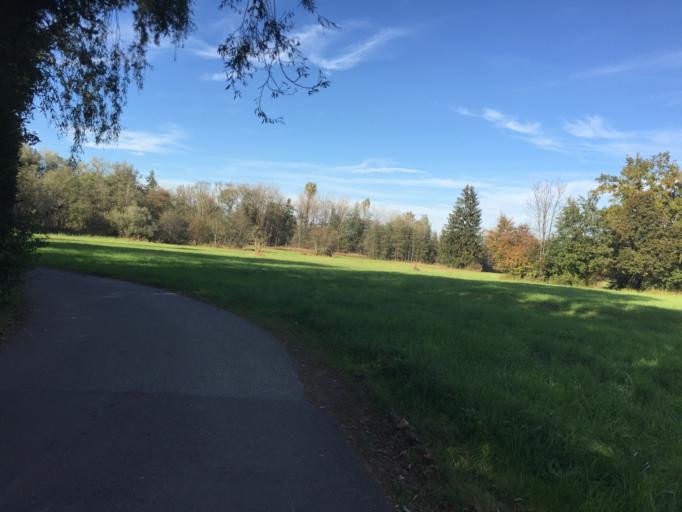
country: AT
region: Salzburg
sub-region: Politischer Bezirk Salzburg-Umgebung
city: Grodig
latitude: 47.7523
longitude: 12.9963
